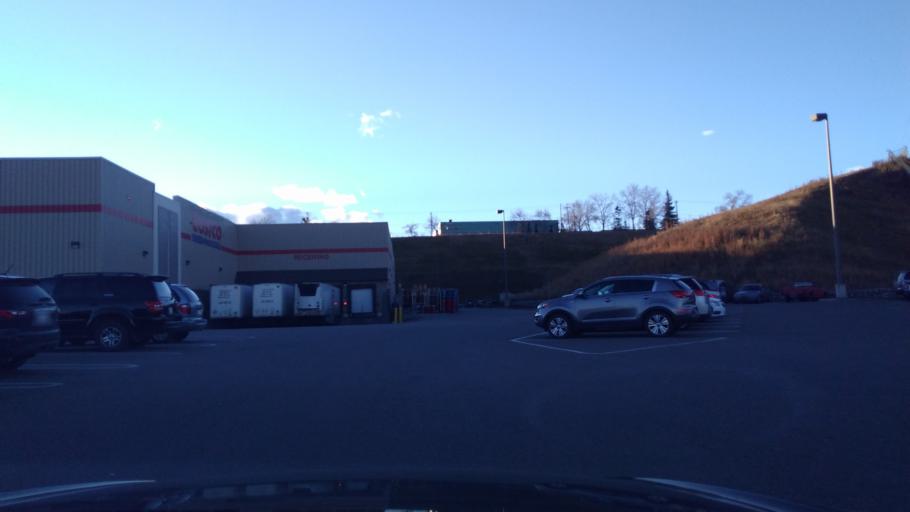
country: CA
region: Alberta
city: Calgary
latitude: 50.9904
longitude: -114.0450
